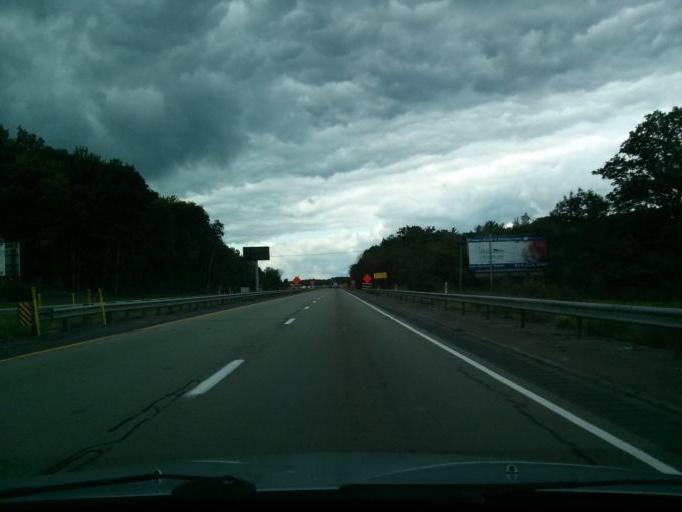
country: US
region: Pennsylvania
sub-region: Jefferson County
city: Brookville
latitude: 41.1892
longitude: -79.2272
